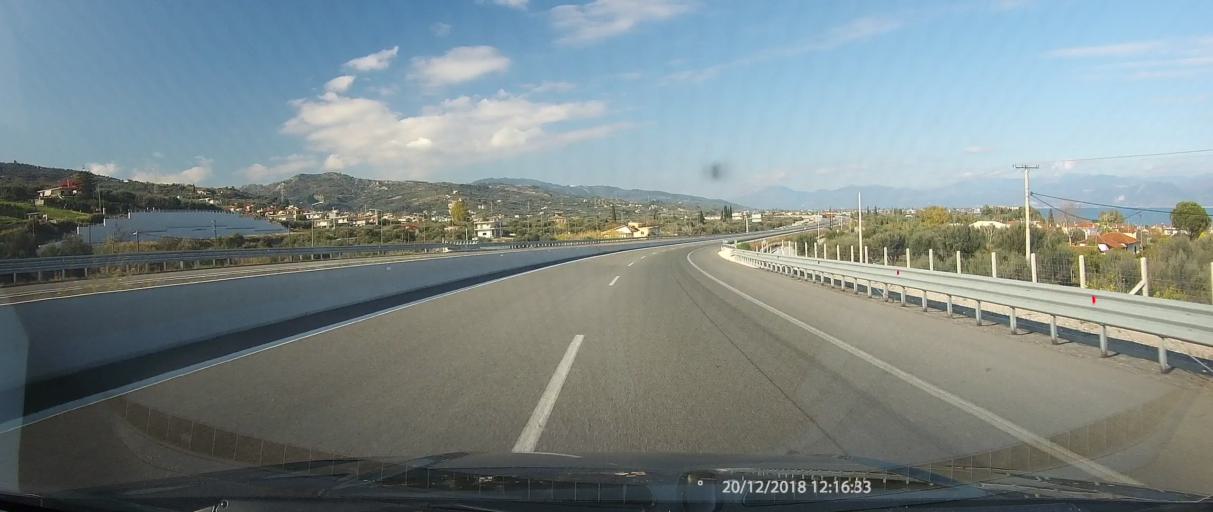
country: GR
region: West Greece
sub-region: Nomos Achaias
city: Selianitika
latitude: 38.2704
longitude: 22.0452
